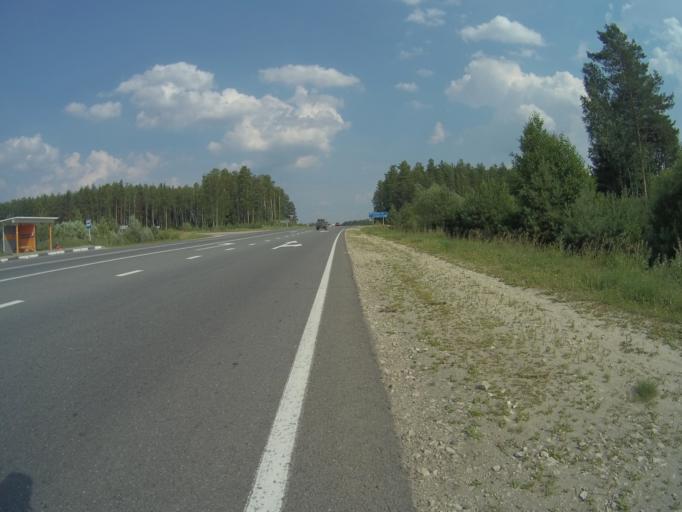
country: RU
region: Vladimir
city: Andreyevo
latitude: 55.9378
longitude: 41.0674
